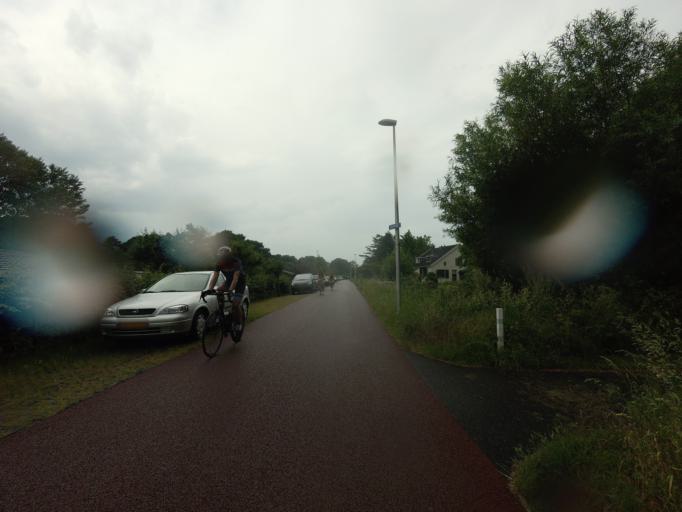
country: NL
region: Utrecht
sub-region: Gemeente Utrecht
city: Utrecht
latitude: 52.1146
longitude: 5.0973
